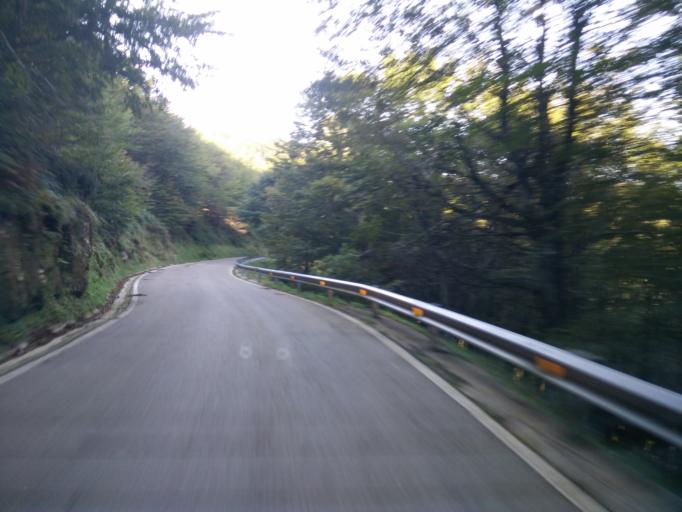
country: ES
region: Cantabria
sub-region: Provincia de Cantabria
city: San Pedro del Romeral
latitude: 43.0536
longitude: -3.8423
